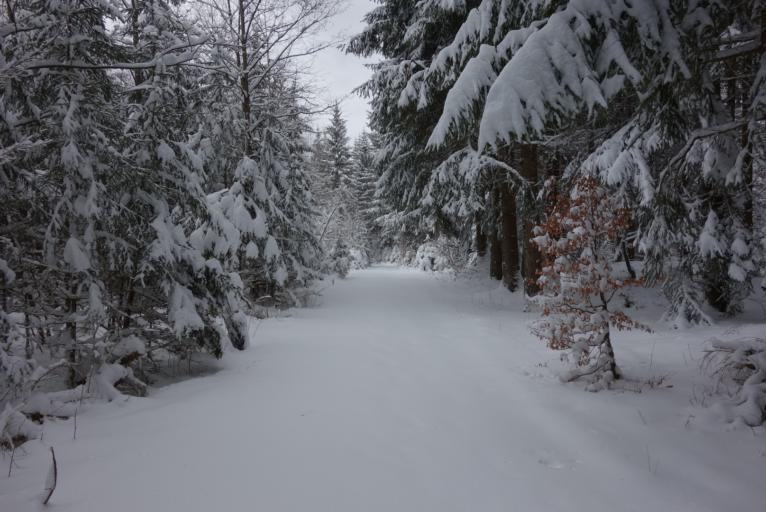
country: DE
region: Saxony
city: Rittersgrun
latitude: 50.4567
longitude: 12.8491
